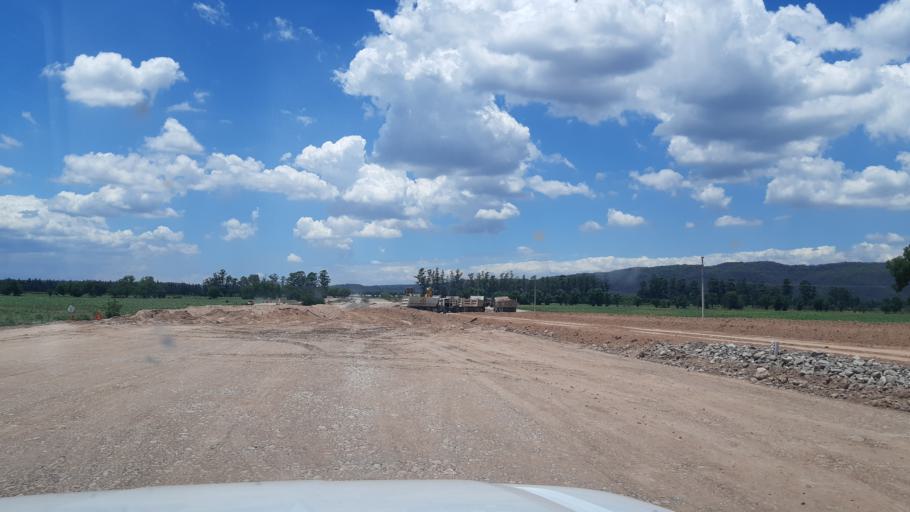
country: AR
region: Jujuy
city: La Mendieta
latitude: -24.4583
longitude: -65.0245
